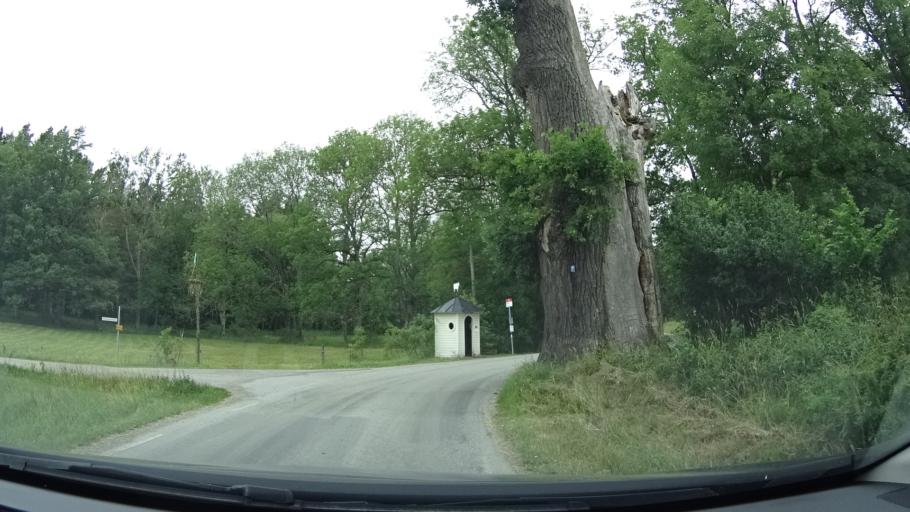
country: SE
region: Stockholm
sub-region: Varmdo Kommun
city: Mortnas
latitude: 59.3794
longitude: 18.4595
